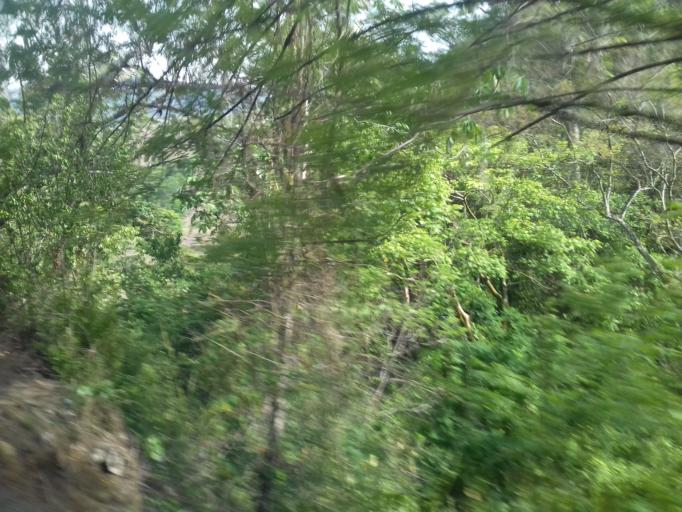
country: CO
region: Antioquia
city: Venecia
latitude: 5.9705
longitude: -75.8276
